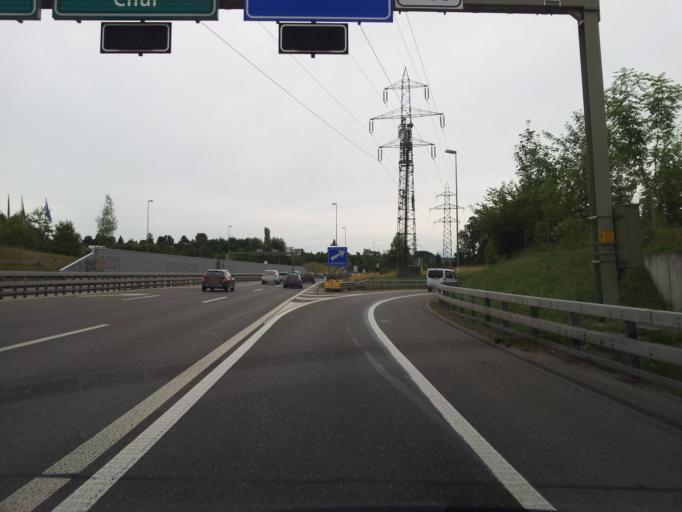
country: CH
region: Zurich
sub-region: Bezirk Zuerich
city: Zuerich (Kreis 2)
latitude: 47.3309
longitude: 8.5280
